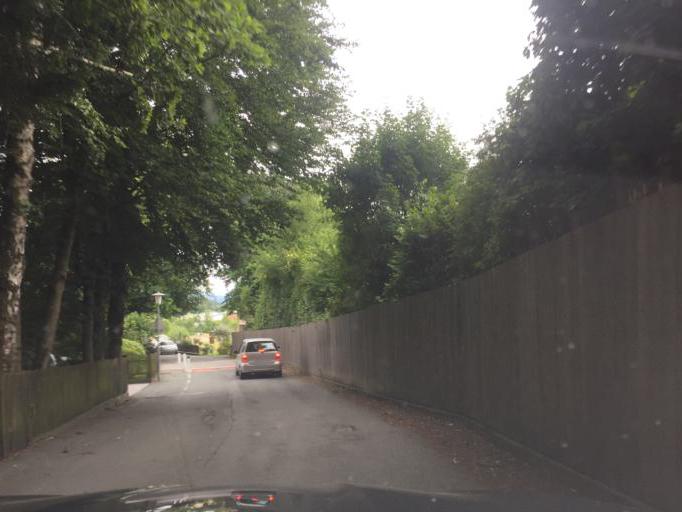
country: AT
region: Styria
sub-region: Politischer Bezirk Graz-Umgebung
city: Hart bei Graz
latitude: 47.0547
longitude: 15.5114
